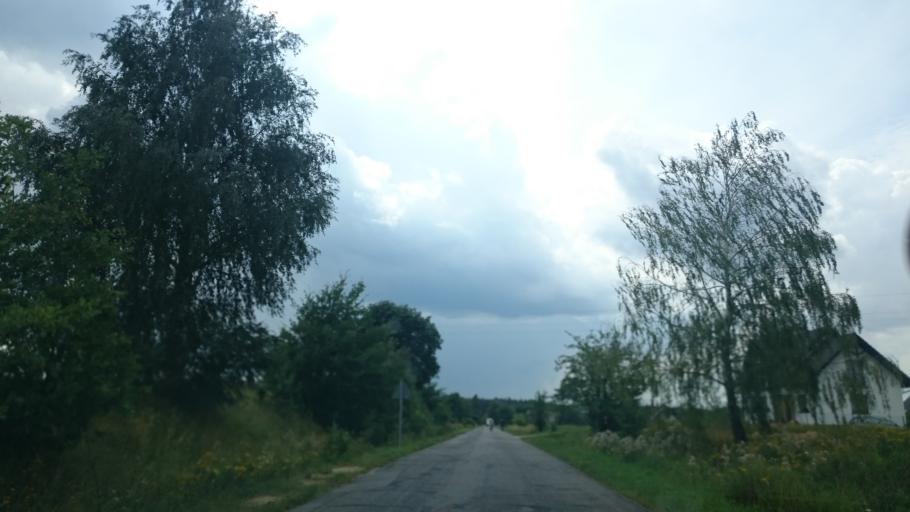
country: PL
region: Pomeranian Voivodeship
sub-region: Powiat chojnicki
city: Chojnice
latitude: 53.6973
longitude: 17.6841
